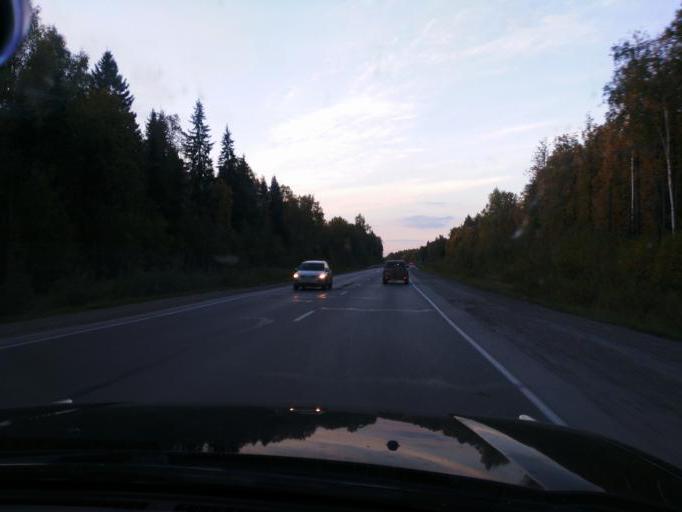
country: RU
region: Perm
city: Polazna
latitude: 58.1312
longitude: 56.4213
